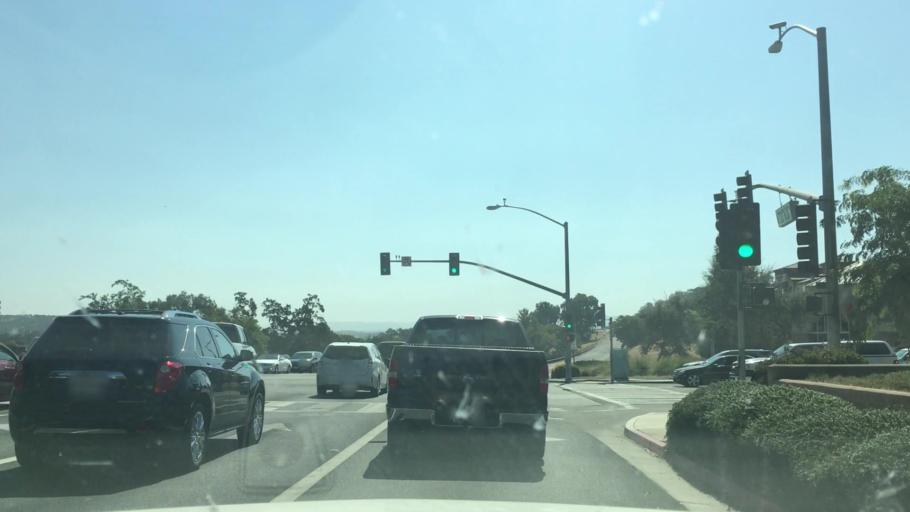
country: US
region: California
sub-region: San Luis Obispo County
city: Paso Robles
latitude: 35.6156
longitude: -120.6906
